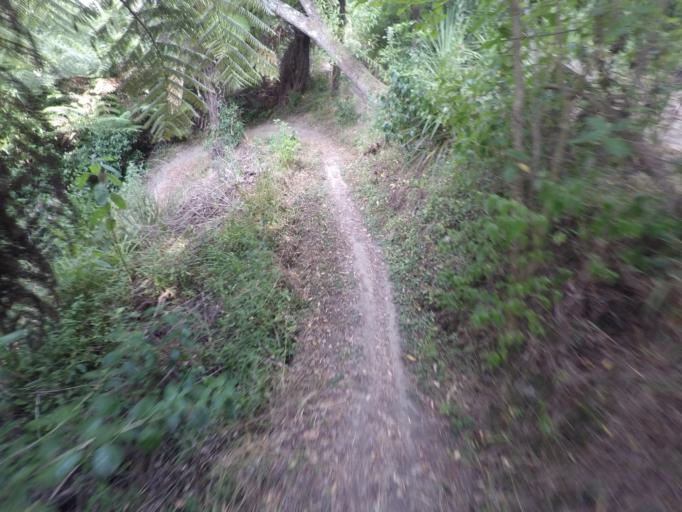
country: NZ
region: Auckland
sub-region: Auckland
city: Auckland
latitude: -36.8681
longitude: 174.7395
